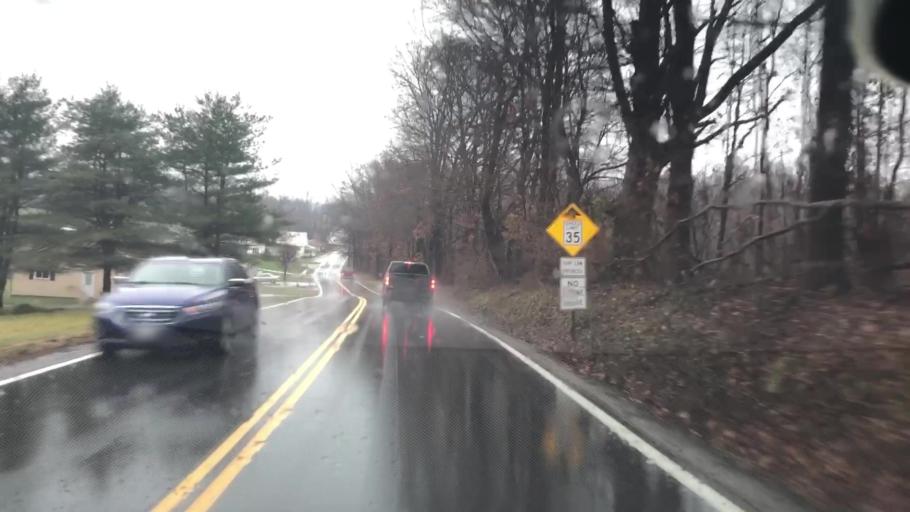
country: US
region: Ohio
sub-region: Harrison County
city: Cadiz
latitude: 40.1915
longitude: -80.9962
